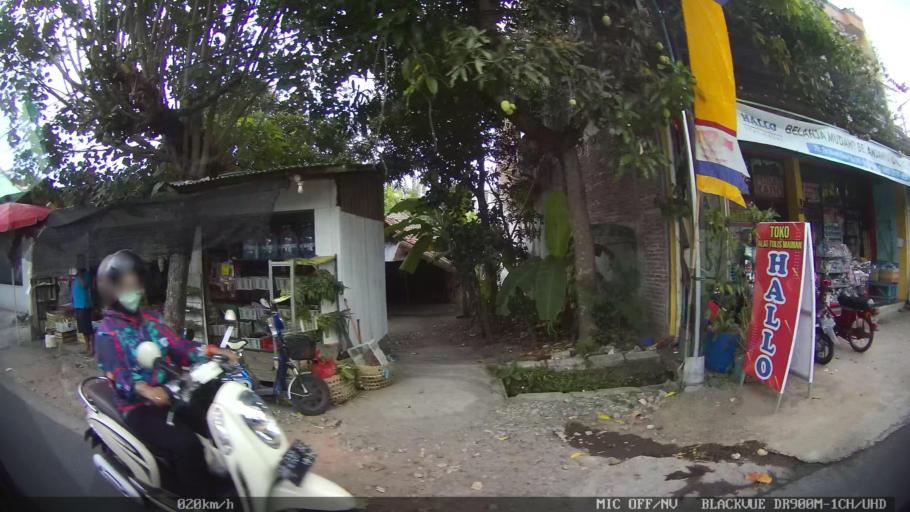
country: ID
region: Daerah Istimewa Yogyakarta
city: Gamping Lor
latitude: -7.7834
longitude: 110.3400
